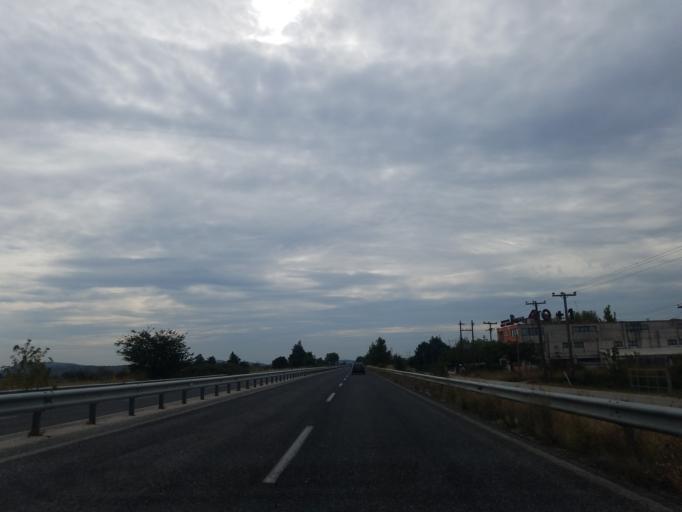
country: GR
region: Thessaly
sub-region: Trikala
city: Vasiliki
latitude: 39.6247
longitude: 21.7087
